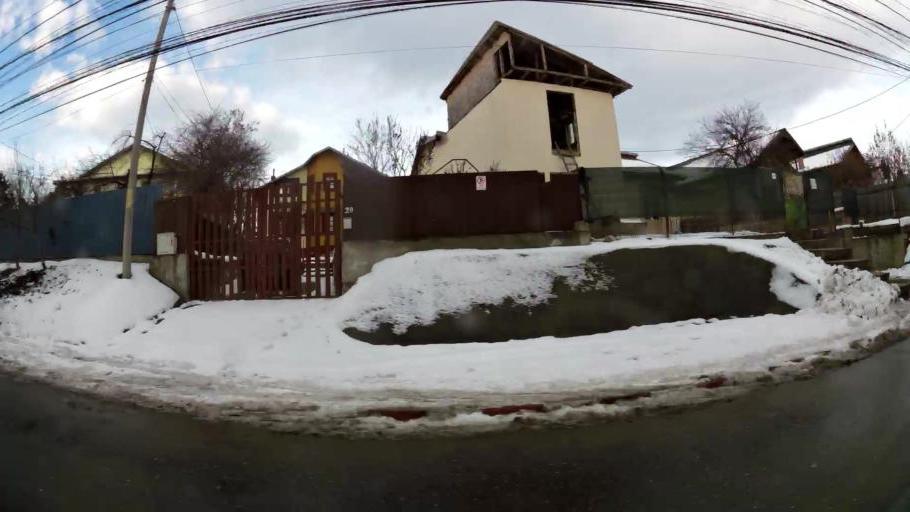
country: RO
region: Ilfov
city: Dobroesti
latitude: 44.4557
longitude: 26.1768
